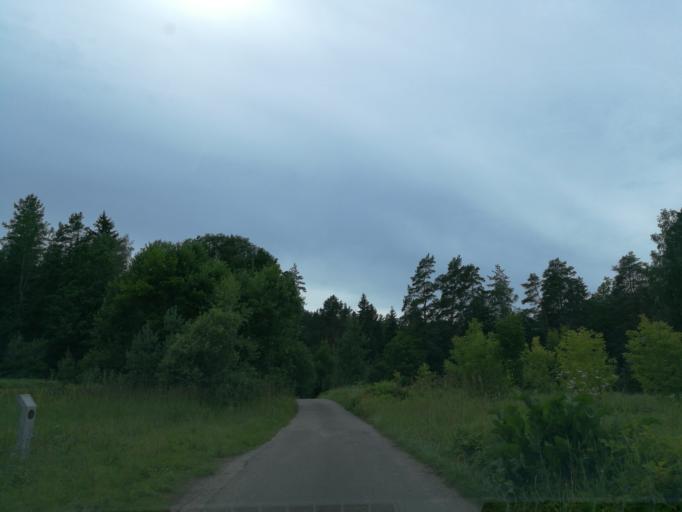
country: LT
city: Grigiskes
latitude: 54.7204
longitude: 25.0458
